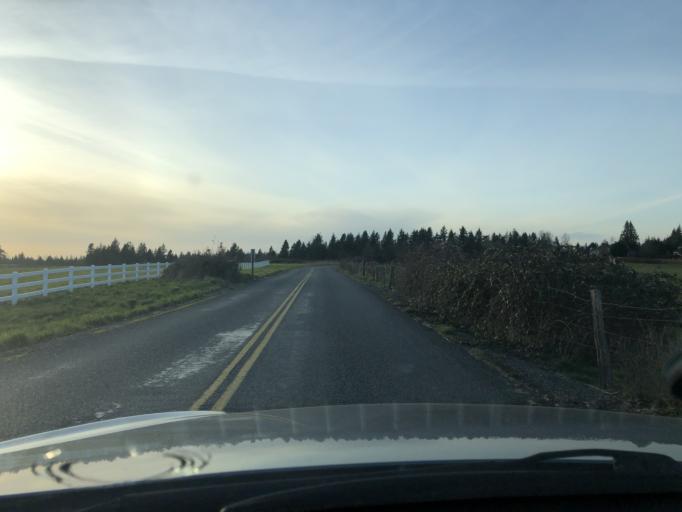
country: US
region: Washington
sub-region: Pierce County
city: Prairie Ridge
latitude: 47.2002
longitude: -122.1191
